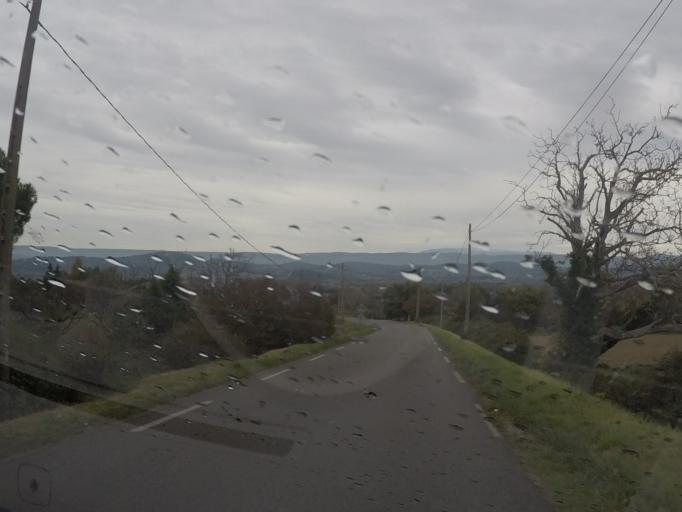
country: FR
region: Provence-Alpes-Cote d'Azur
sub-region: Departement du Vaucluse
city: Bonnieux
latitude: 43.8337
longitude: 5.2951
